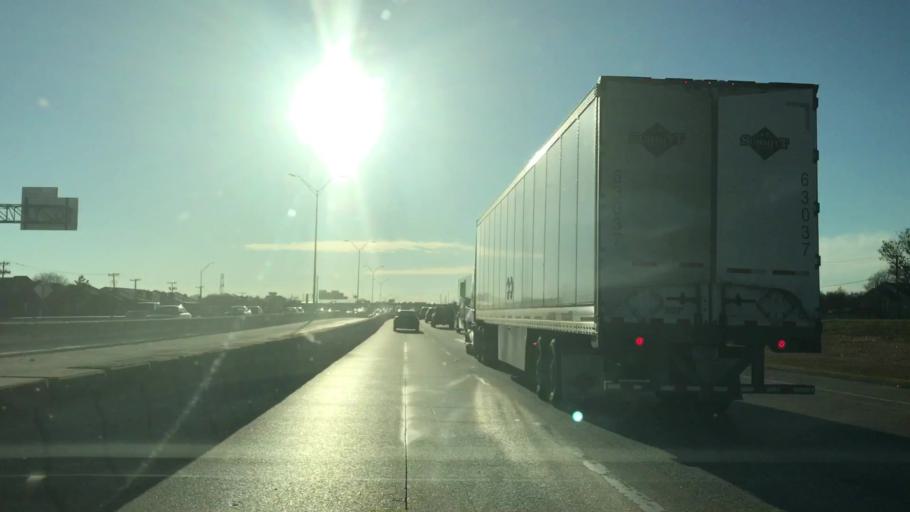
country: US
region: Texas
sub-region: Dallas County
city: Mesquite
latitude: 32.8215
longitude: -96.6327
